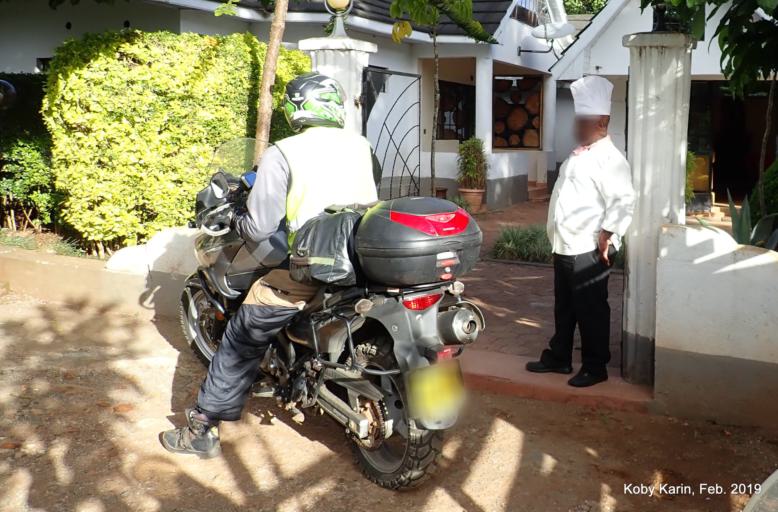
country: KE
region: Kericho
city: Kericho
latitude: -0.3652
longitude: 35.2950
